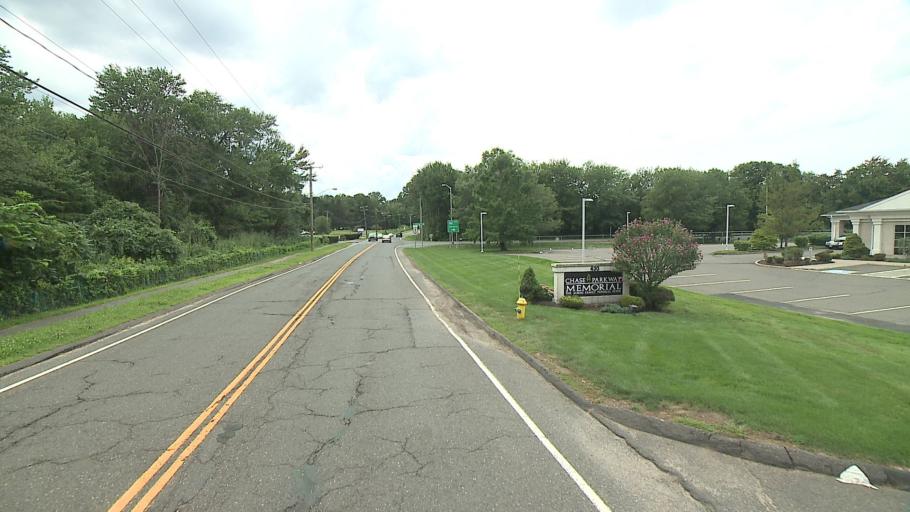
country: US
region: Connecticut
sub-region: New Haven County
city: Waterbury
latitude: 41.5475
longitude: -73.0610
